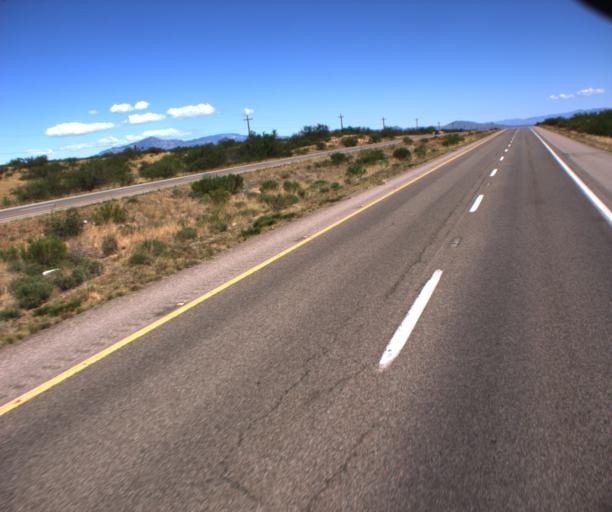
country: US
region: Arizona
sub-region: Cochise County
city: Whetstone
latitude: 31.8877
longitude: -110.3410
